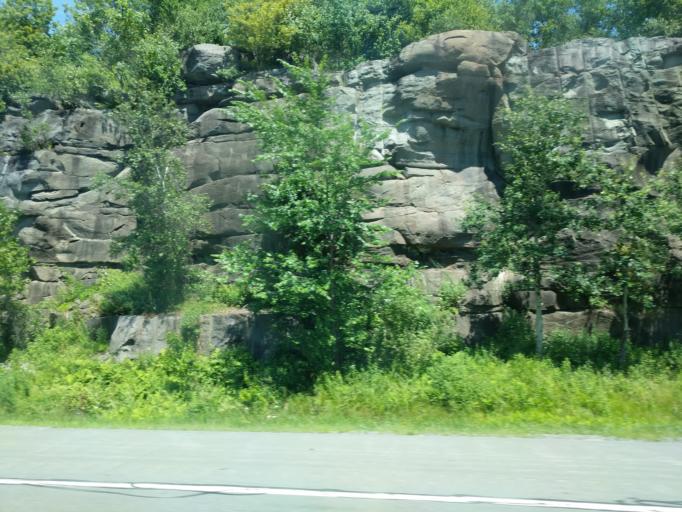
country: US
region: New York
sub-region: Sullivan County
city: Rock Hill
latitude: 41.6313
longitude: -74.6114
